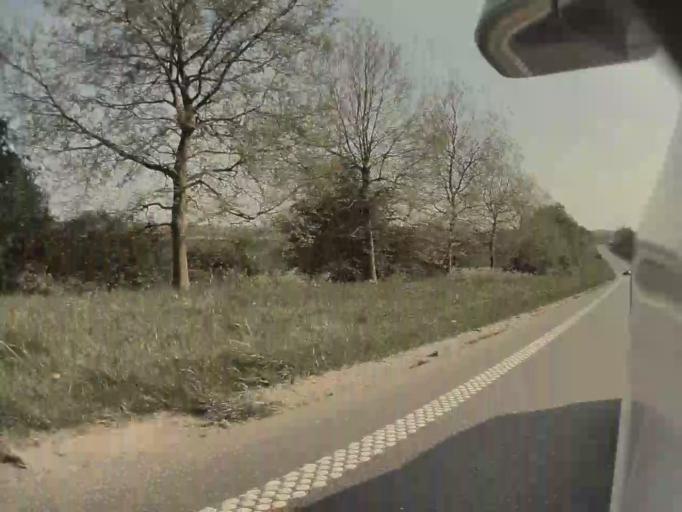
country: BE
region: Wallonia
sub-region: Province de Namur
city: Ciney
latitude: 50.3080
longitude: 5.1225
